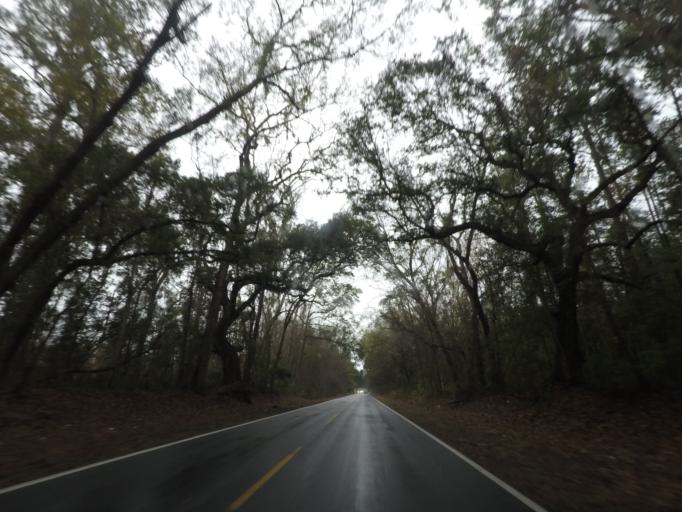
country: US
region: South Carolina
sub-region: Charleston County
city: Meggett
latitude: 32.6904
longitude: -80.3499
